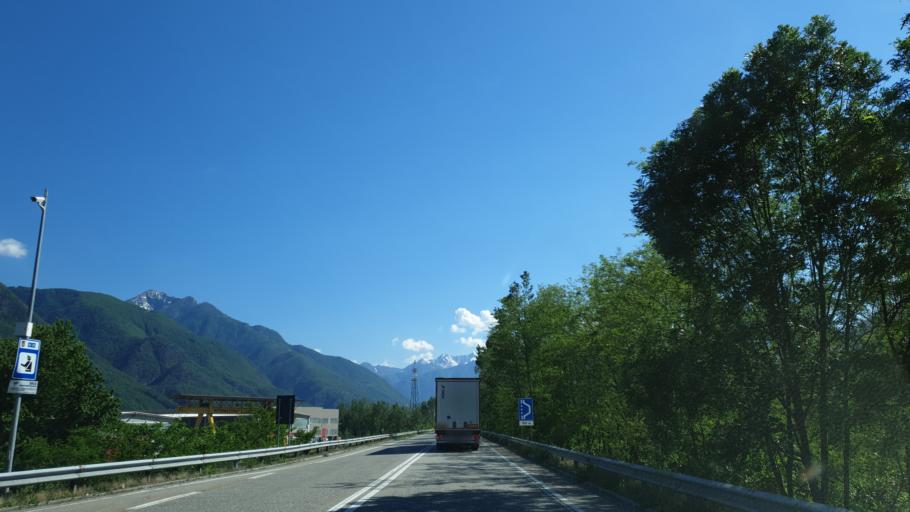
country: IT
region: Piedmont
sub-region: Provincia Verbano-Cusio-Ossola
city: Domodossola
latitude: 46.1214
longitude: 8.3071
